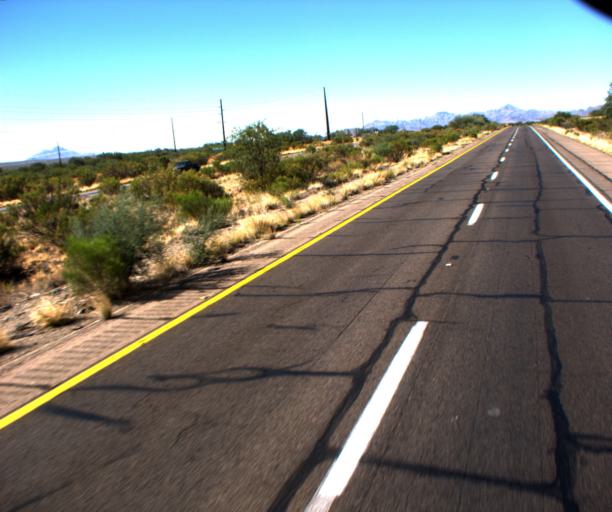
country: US
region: Arizona
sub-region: Pima County
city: Arivaca Junction
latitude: 31.7510
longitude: -111.0438
